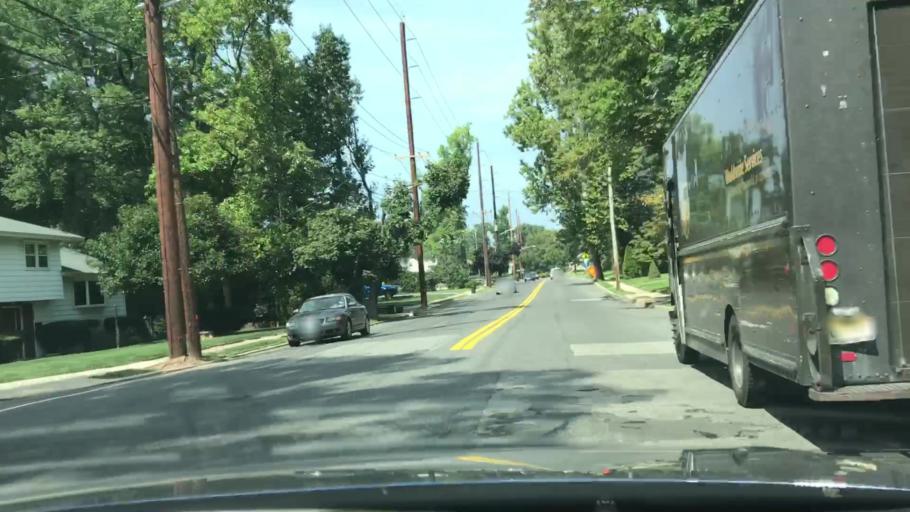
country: US
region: New Jersey
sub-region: Bergen County
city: New Milford
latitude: 40.9198
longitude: -74.0176
